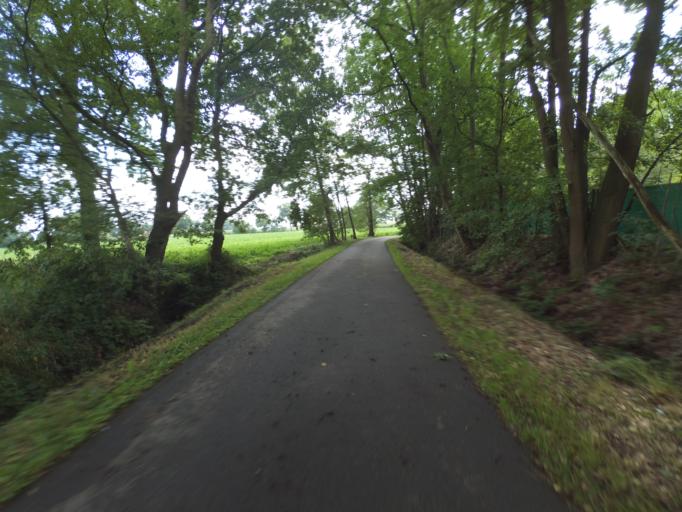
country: BE
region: Flanders
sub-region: Provincie Limburg
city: Kinrooi
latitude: 51.1190
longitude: 5.7463
